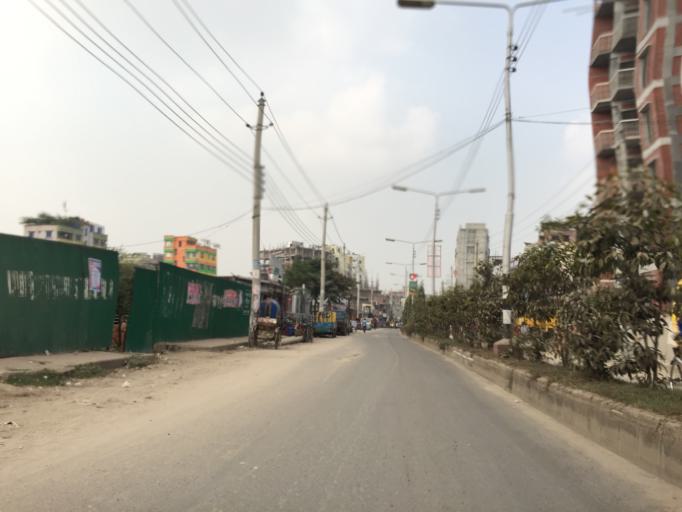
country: BD
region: Dhaka
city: Azimpur
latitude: 23.7833
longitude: 90.3683
